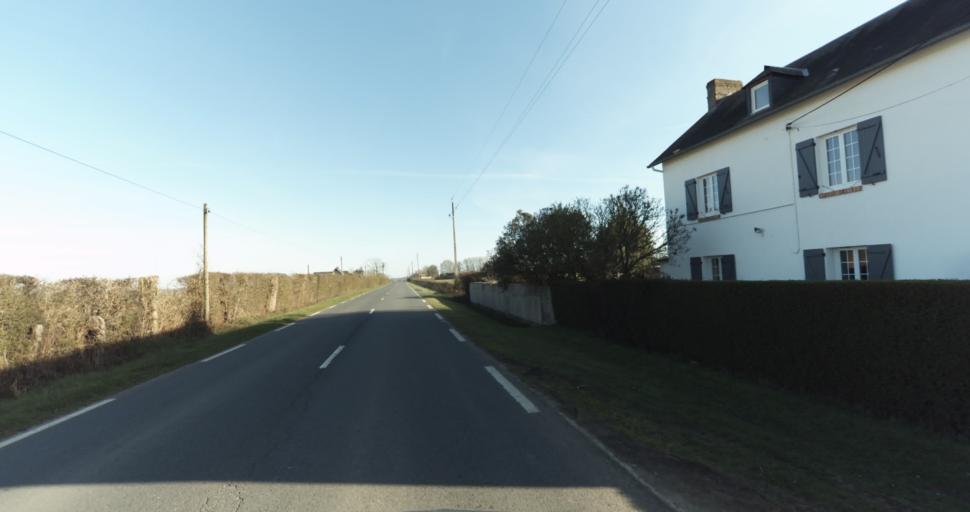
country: FR
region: Lower Normandy
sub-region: Departement du Calvados
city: Livarot
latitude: 48.9996
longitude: 0.1101
